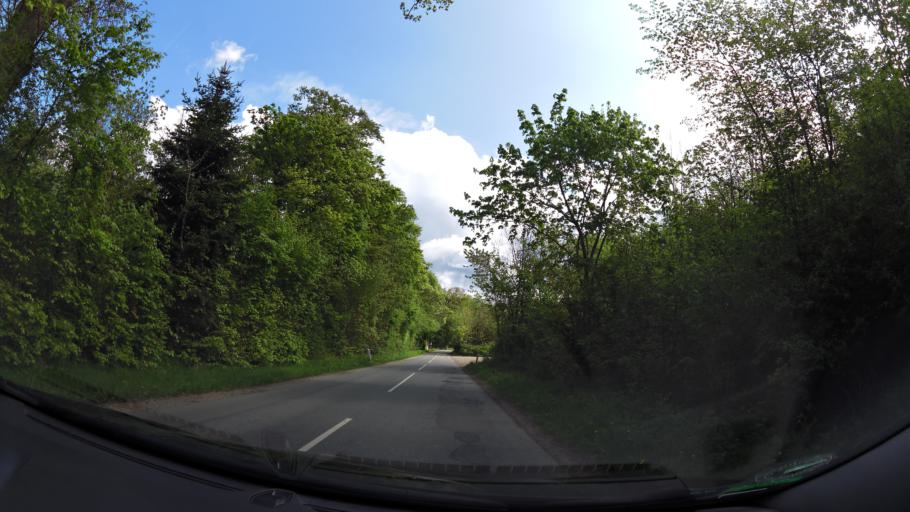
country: DK
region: South Denmark
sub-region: Svendborg Kommune
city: Thuro By
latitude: 55.1424
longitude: 10.7478
